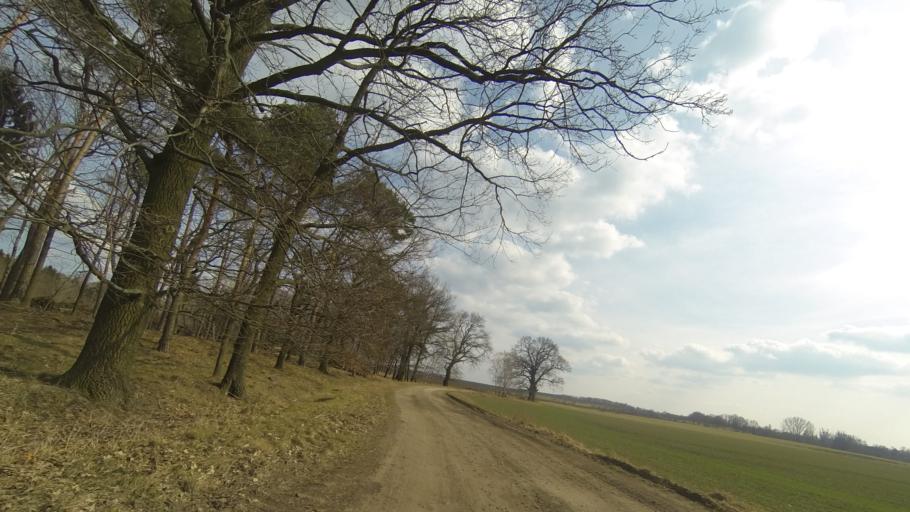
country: DE
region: Saxony
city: Radeburg
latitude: 51.2473
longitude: 13.7036
